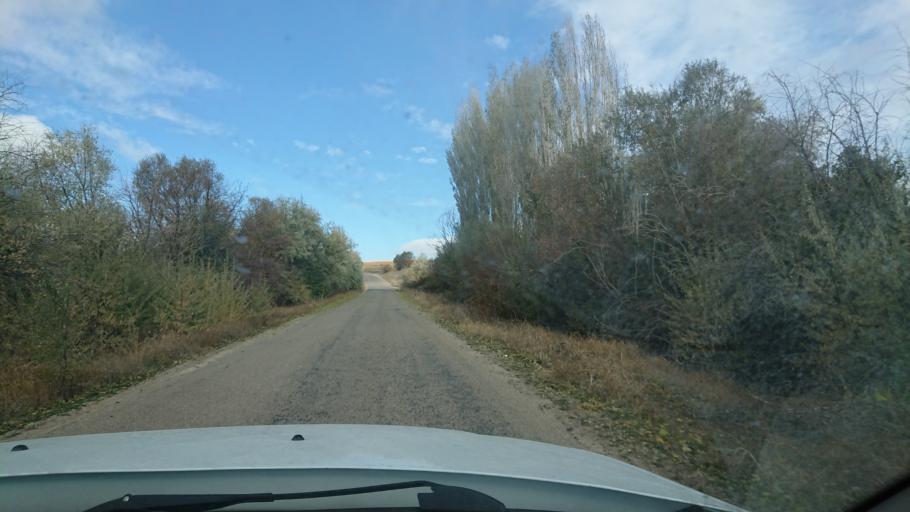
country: TR
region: Aksaray
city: Agacoren
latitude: 38.8319
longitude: 33.9559
